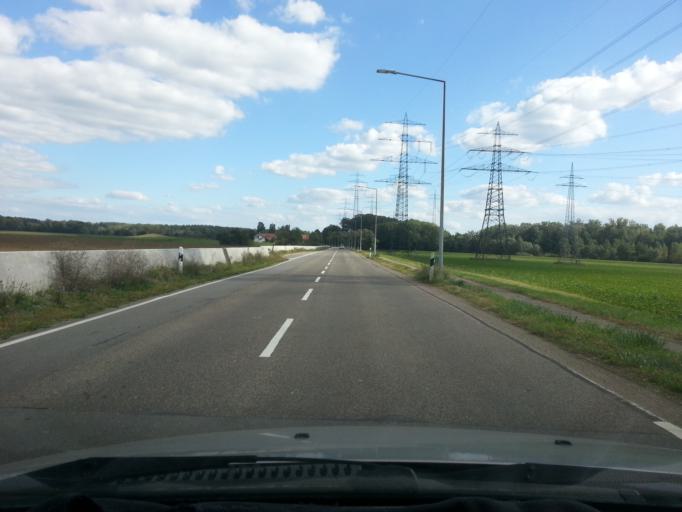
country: DE
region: Baden-Wuerttemberg
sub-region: Karlsruhe Region
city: Philippsburg
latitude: 49.2493
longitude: 8.4460
